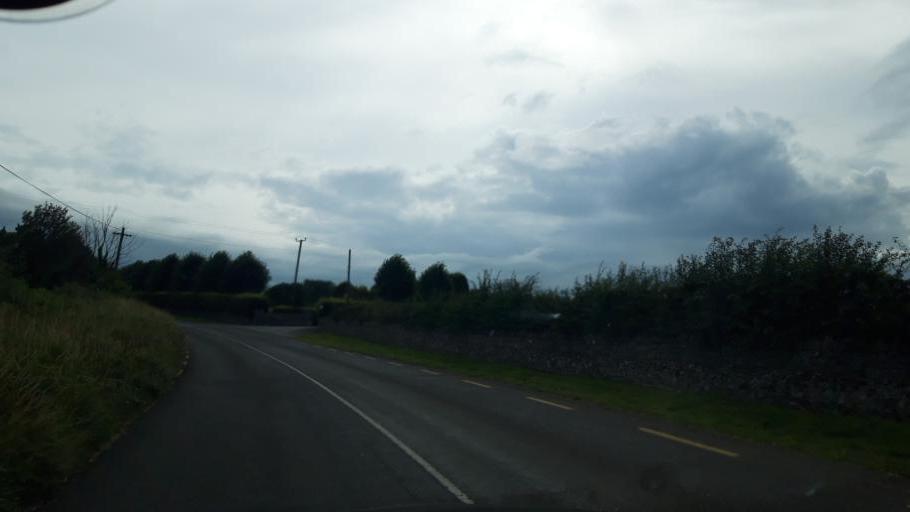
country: IE
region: Leinster
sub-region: Kilkenny
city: Ballyragget
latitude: 52.7639
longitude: -7.3617
